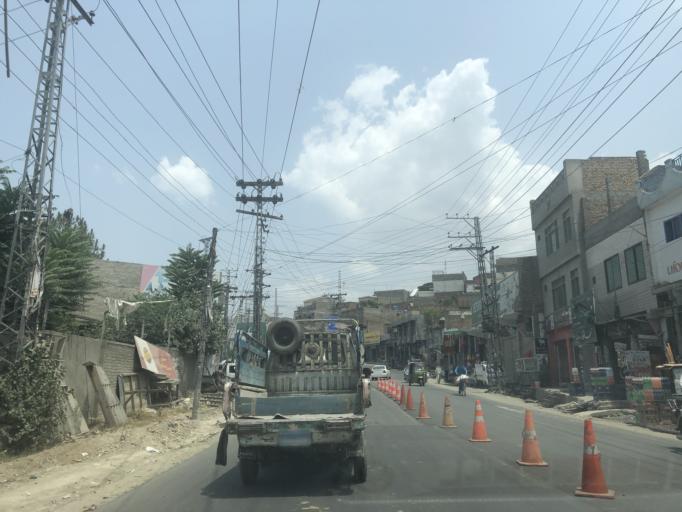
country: PK
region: Khyber Pakhtunkhwa
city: Mingora
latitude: 34.7714
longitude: 72.3471
